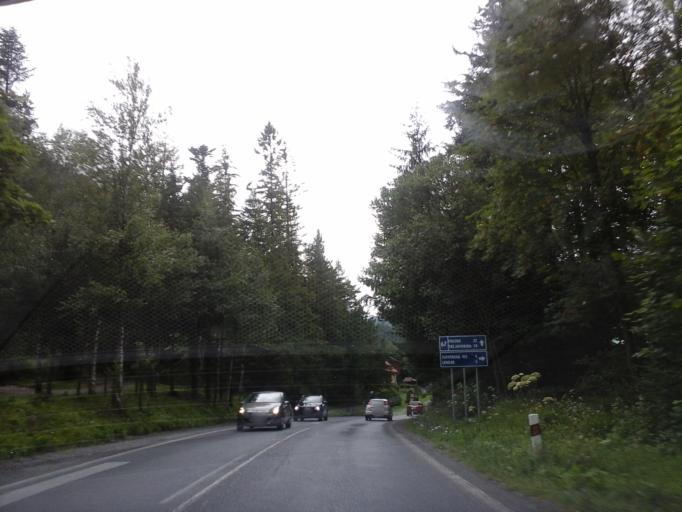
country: SK
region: Presovsky
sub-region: Okres Poprad
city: Zdiar
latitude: 49.2299
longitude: 20.3169
